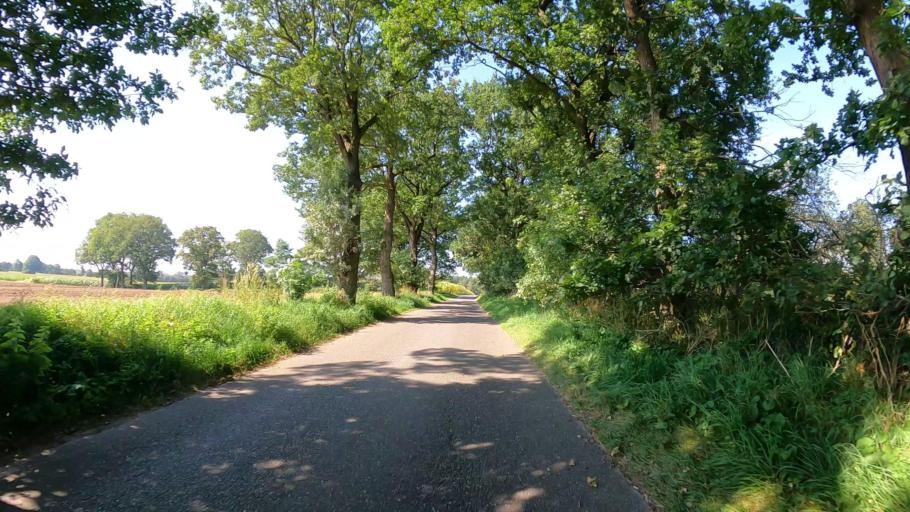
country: DE
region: Schleswig-Holstein
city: Nutzen
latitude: 53.8682
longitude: 9.9089
